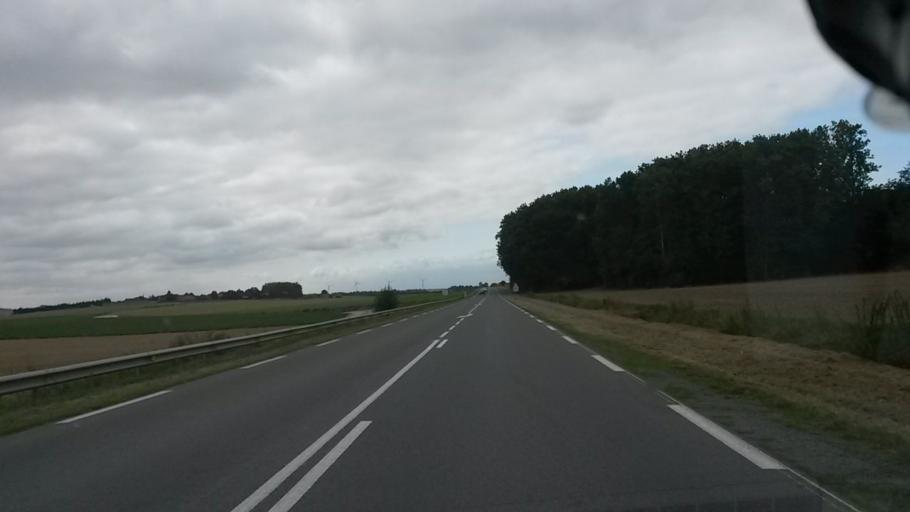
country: FR
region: Nord-Pas-de-Calais
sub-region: Departement du Nord
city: Fontaine-Notre-Dame
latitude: 50.1629
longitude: 3.1417
